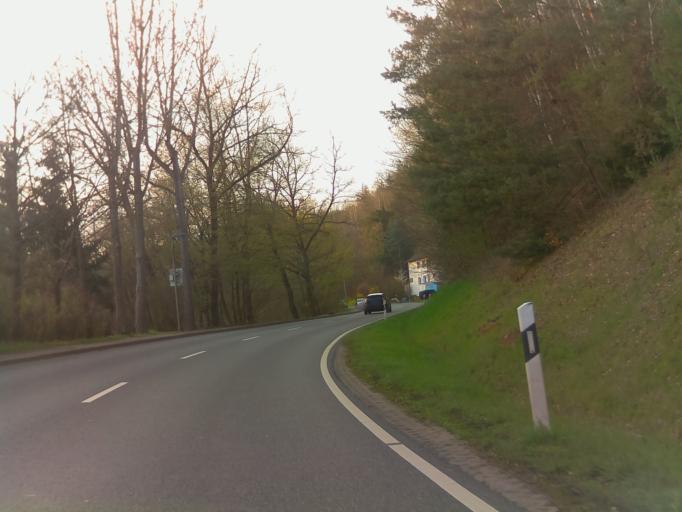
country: DE
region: Hesse
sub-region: Regierungsbezirk Kassel
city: Friedewald
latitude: 50.8645
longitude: 9.9096
